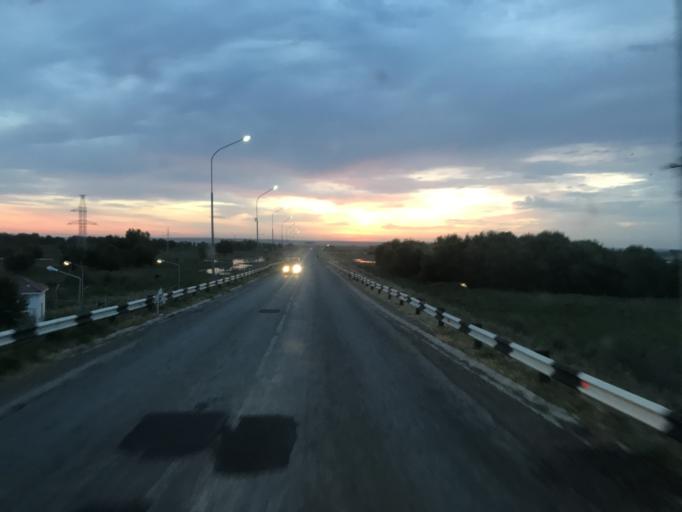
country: KZ
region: Ongtustik Qazaqstan
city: Ilyich
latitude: 41.0307
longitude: 68.5200
